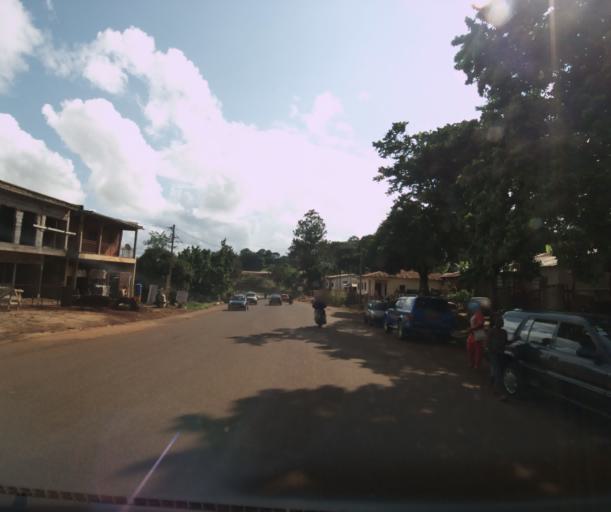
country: CM
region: West
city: Foumban
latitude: 5.7314
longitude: 10.8745
